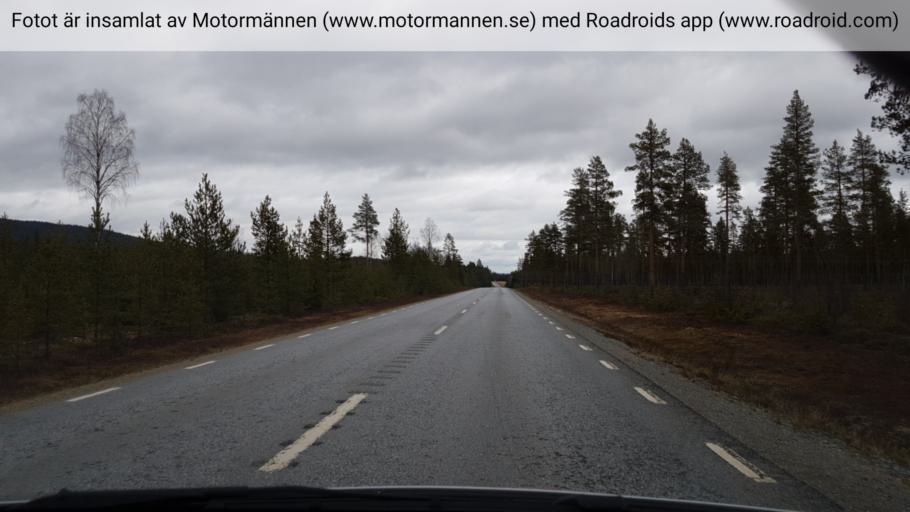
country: SE
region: Vaesterbotten
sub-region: Bjurholms Kommun
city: Bjurholm
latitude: 63.9291
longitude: 19.0053
